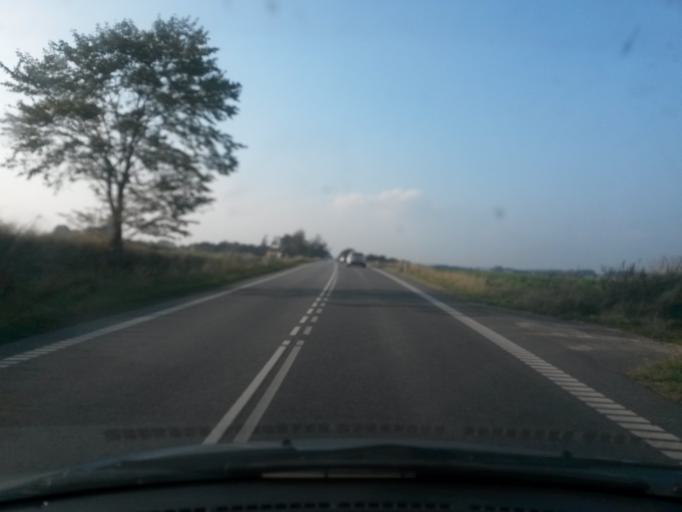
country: DK
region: Central Jutland
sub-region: Syddjurs Kommune
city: Hornslet
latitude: 56.3762
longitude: 10.3074
